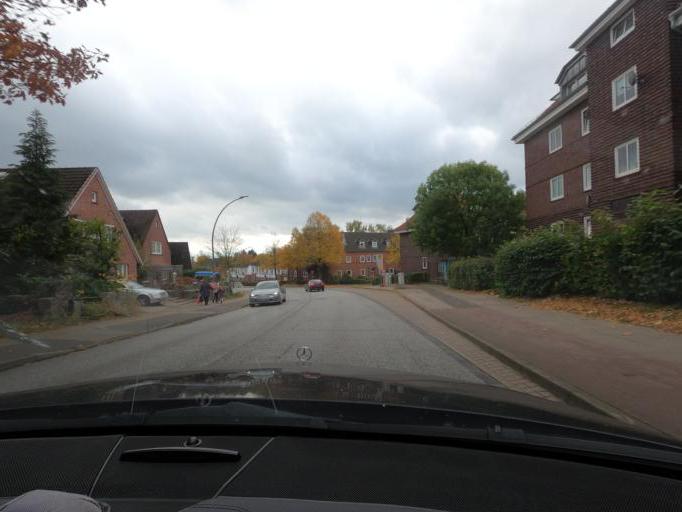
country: DE
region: Schleswig-Holstein
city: Geesthacht
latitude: 53.4428
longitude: 10.3717
